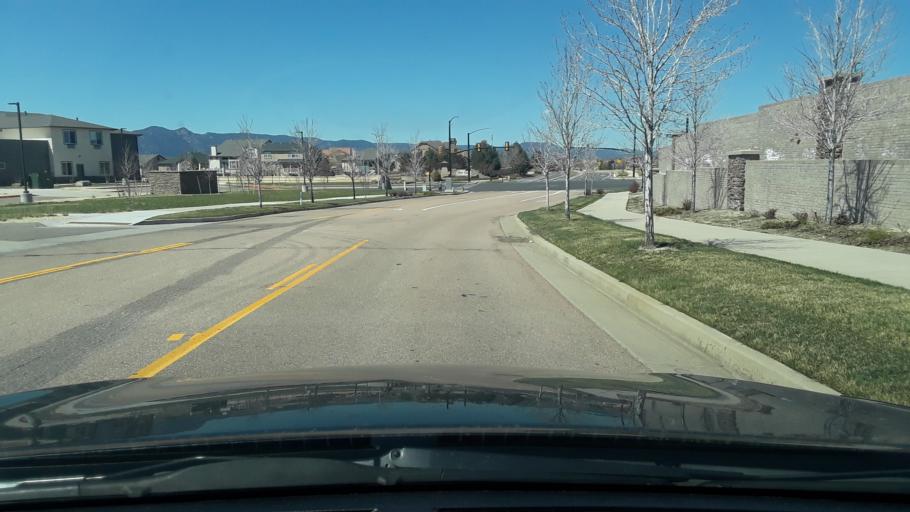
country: US
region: Colorado
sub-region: El Paso County
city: Black Forest
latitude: 38.9702
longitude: -104.7504
